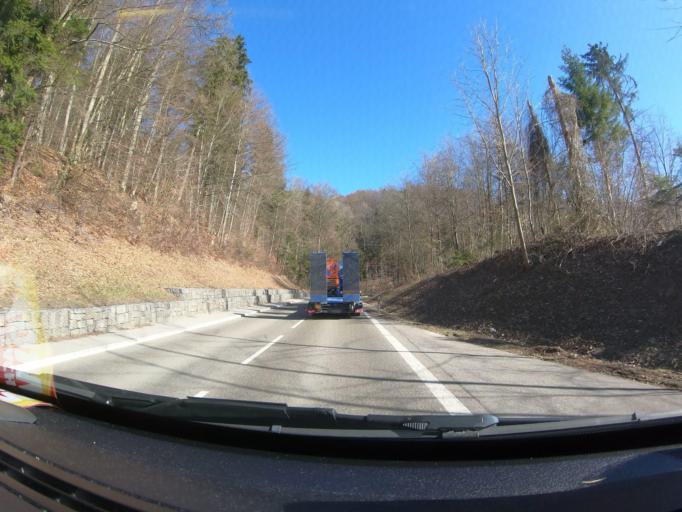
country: DE
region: Baden-Wuerttemberg
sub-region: Regierungsbezirk Stuttgart
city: Gaildorf
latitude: 49.0140
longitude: 9.7854
